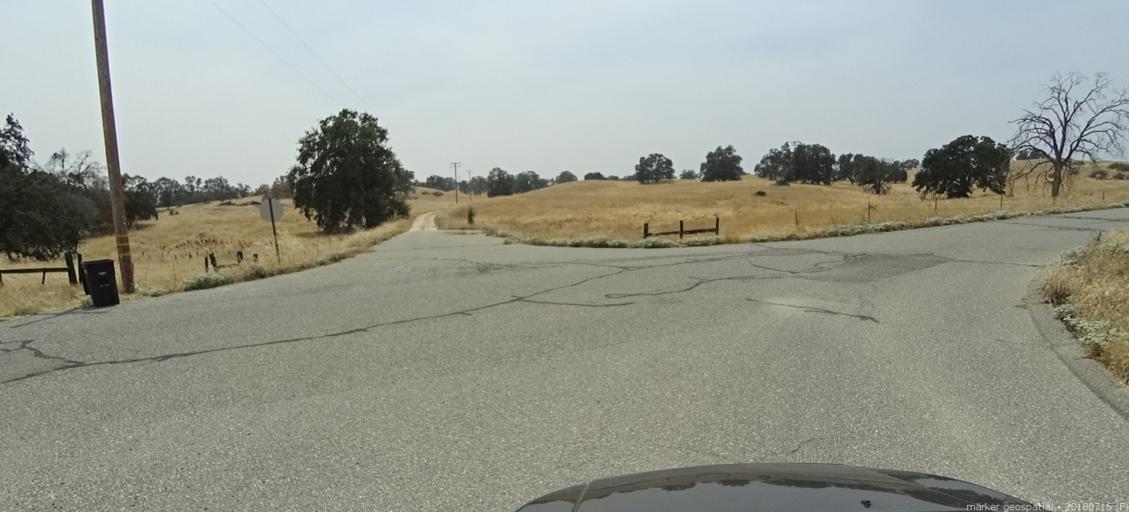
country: US
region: California
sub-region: Madera County
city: Yosemite Lakes
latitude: 37.1910
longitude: -119.9042
